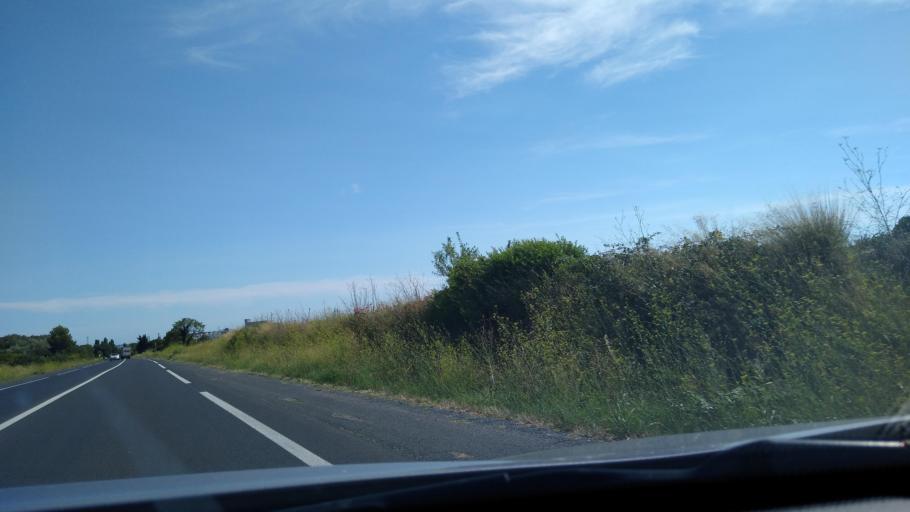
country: FR
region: Languedoc-Roussillon
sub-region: Departement de l'Herault
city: Frontignan
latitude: 43.4290
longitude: 3.7217
